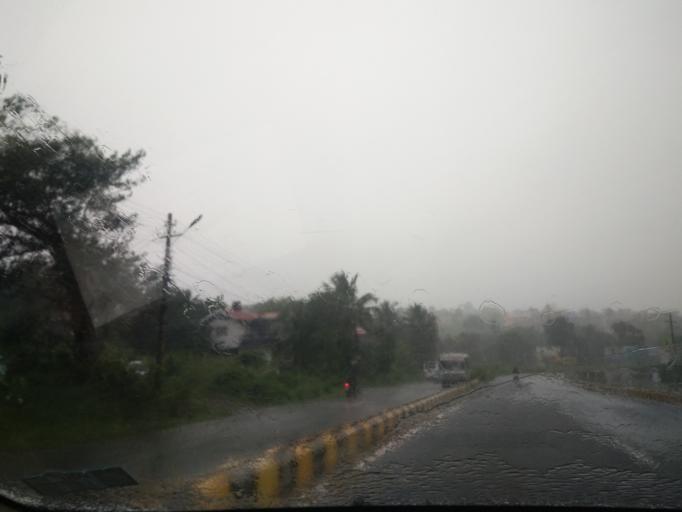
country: IN
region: Goa
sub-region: North Goa
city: Bambolim
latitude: 15.4647
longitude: 73.8539
